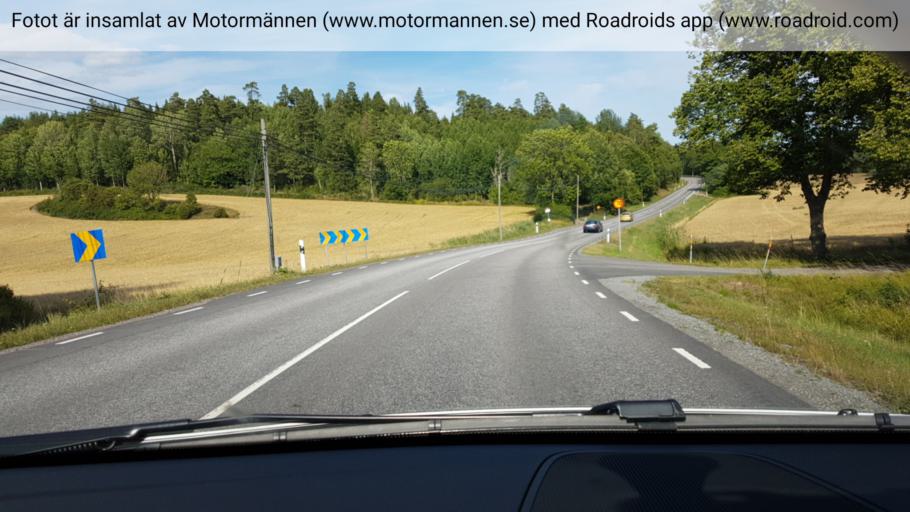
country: SE
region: Stockholm
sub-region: Sodertalje Kommun
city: Pershagen
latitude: 59.1008
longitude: 17.6264
